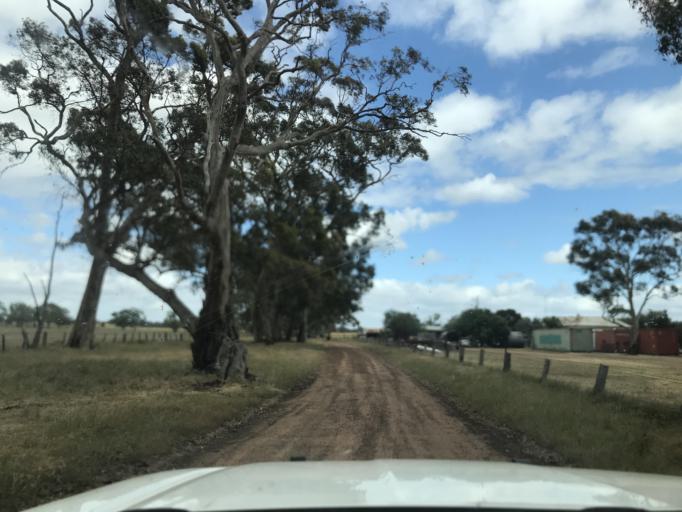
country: AU
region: South Australia
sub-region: Naracoorte and Lucindale
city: Naracoorte
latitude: -36.8993
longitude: 141.3896
